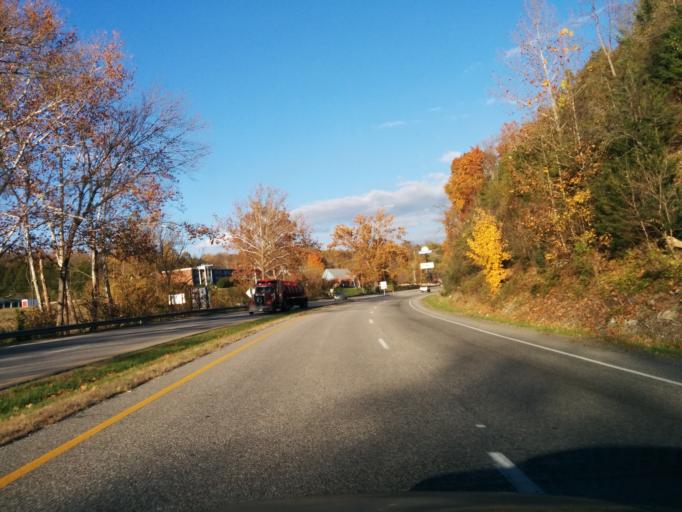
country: US
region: Virginia
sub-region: Rockbridge County
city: East Lexington
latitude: 37.8376
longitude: -79.3749
